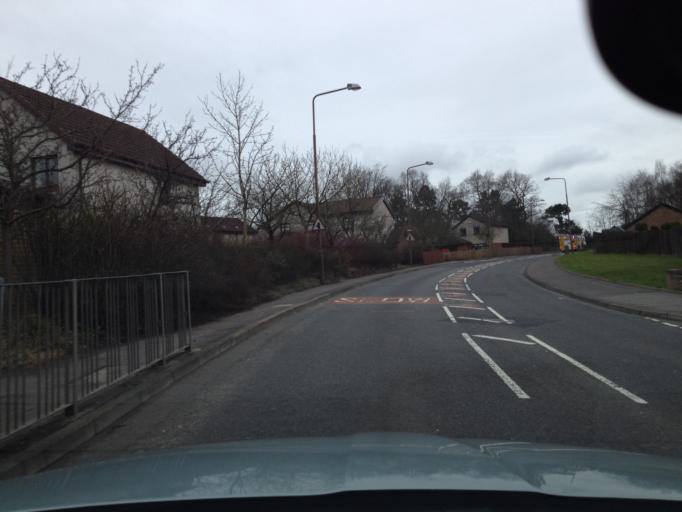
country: GB
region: Scotland
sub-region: West Lothian
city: Mid Calder
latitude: 55.8825
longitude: -3.4883
